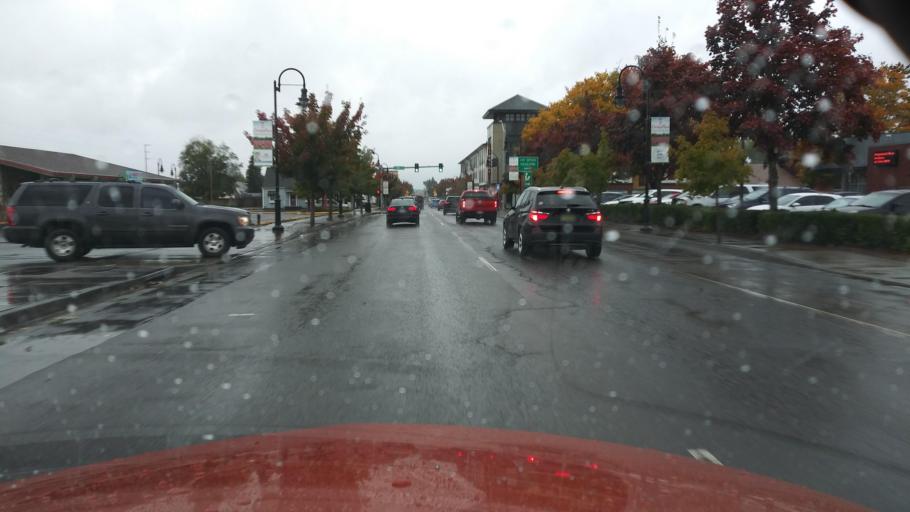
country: US
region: Oregon
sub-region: Washington County
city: Cornelius
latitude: 45.5209
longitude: -123.0535
